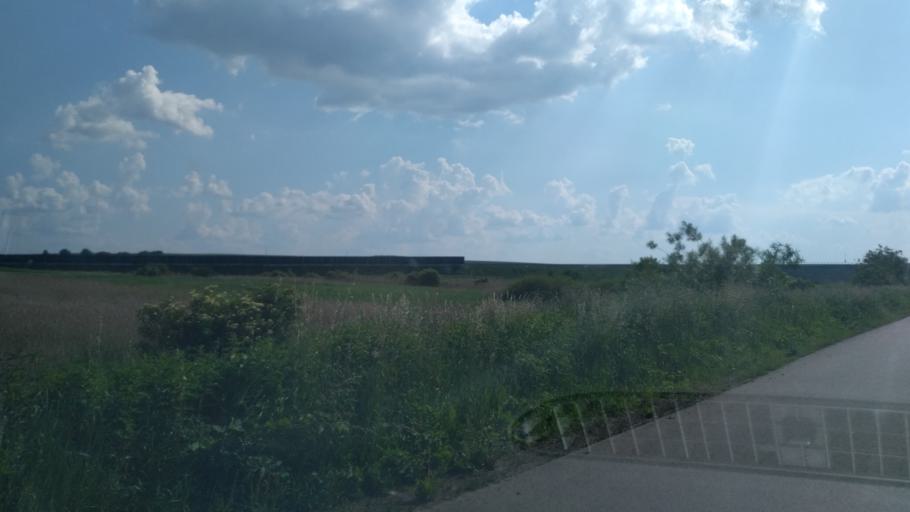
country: PL
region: Subcarpathian Voivodeship
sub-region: Powiat jaroslawski
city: Ostrow
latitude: 49.9267
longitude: 22.7334
